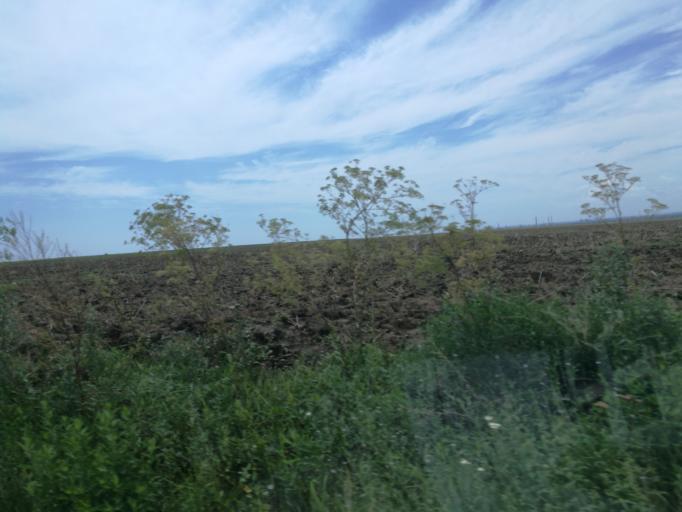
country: RO
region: Constanta
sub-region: Comuna Corbu
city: Corbu
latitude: 44.4239
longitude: 28.6755
